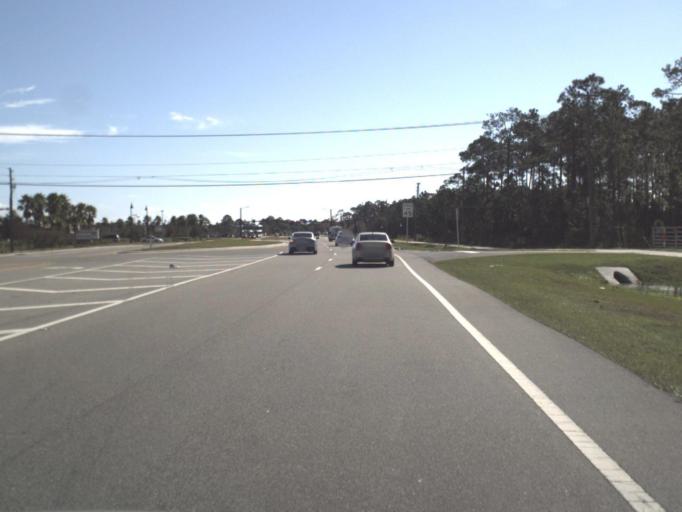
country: US
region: Florida
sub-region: Volusia County
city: Port Orange
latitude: 29.1105
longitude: -81.0388
